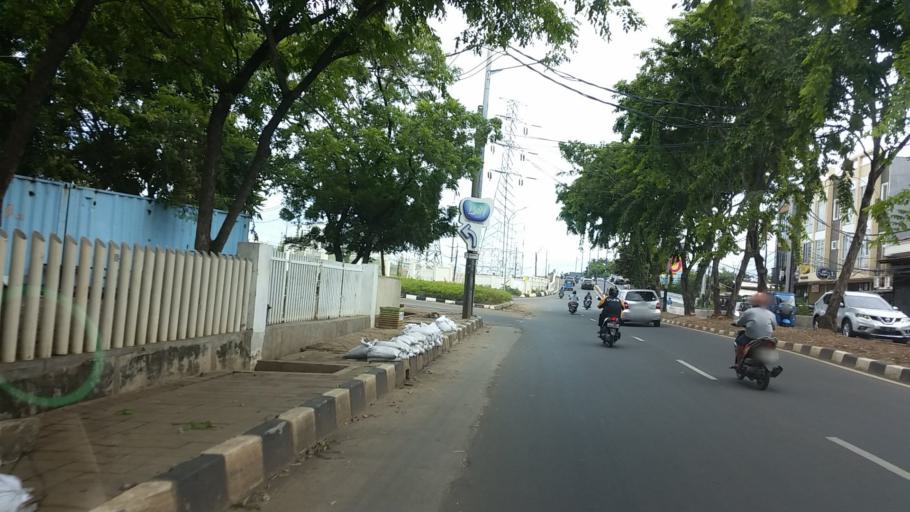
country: ID
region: Jakarta Raya
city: Jakarta
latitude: -6.1123
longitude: 106.7835
